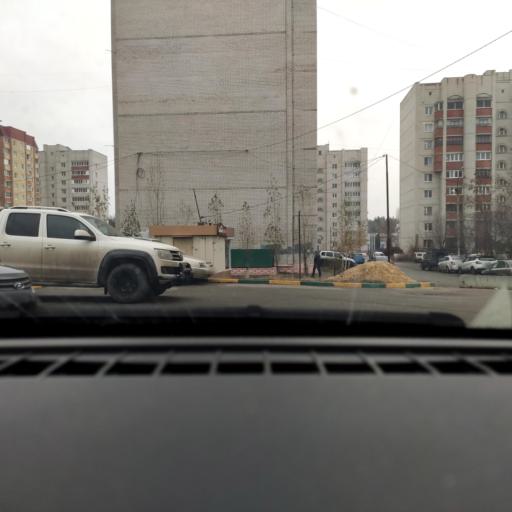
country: RU
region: Voronezj
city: Shilovo
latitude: 51.5606
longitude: 39.1166
